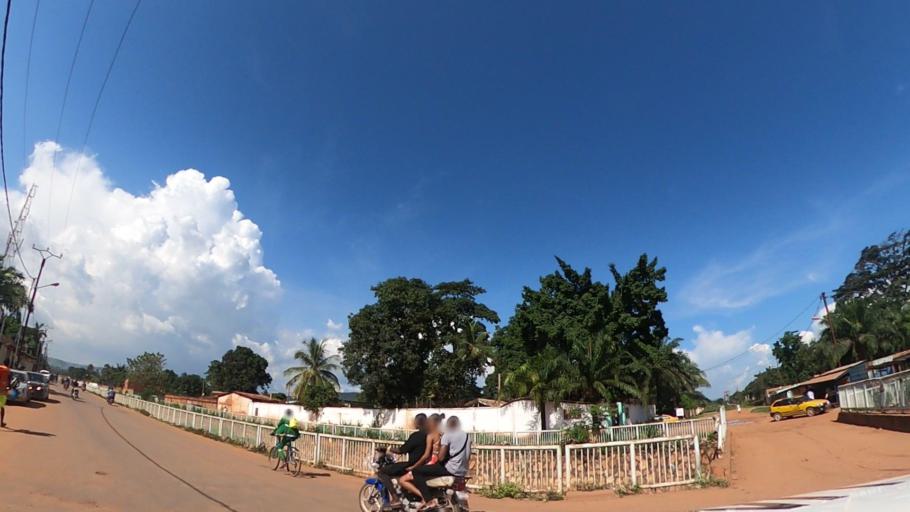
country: CF
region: Bangui
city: Bangui
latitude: 4.3694
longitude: 18.5521
